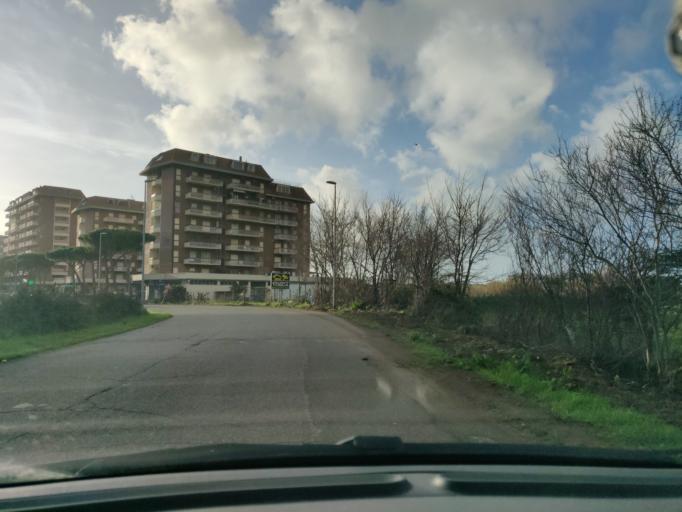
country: IT
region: Latium
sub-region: Provincia di Viterbo
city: Tarquinia
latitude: 42.2253
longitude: 11.7101
